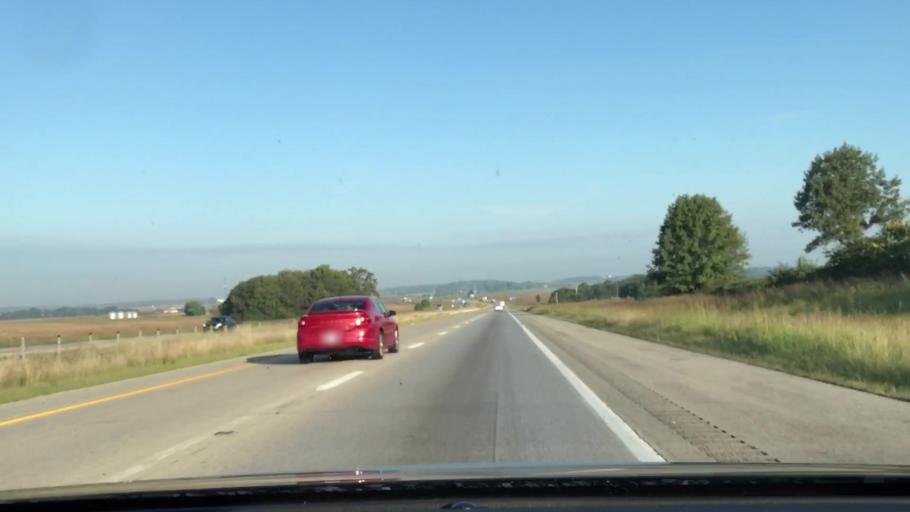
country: US
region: Kentucky
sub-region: Christian County
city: Oak Grove
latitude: 36.6714
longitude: -87.3881
